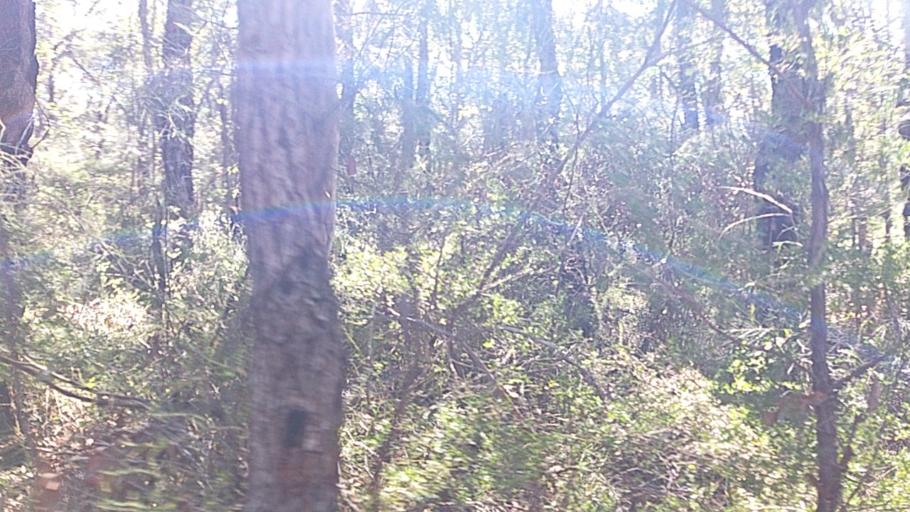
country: AU
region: New South Wales
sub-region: Ryde
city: East Ryde
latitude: -33.8148
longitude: 151.1313
